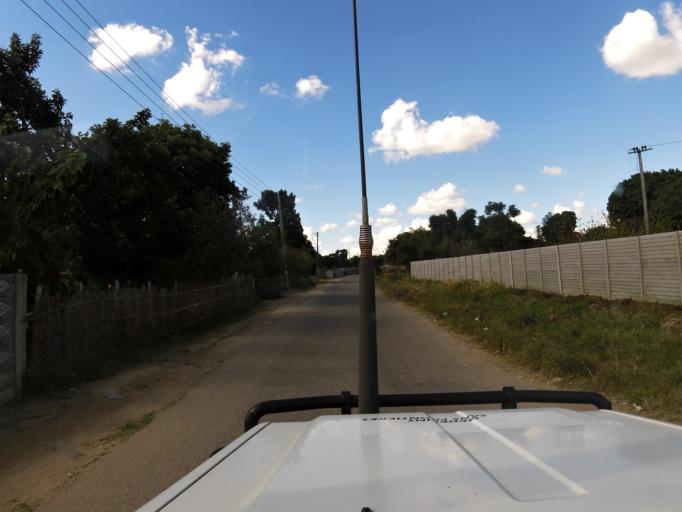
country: ZW
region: Harare
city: Epworth
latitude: -17.8717
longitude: 31.1297
